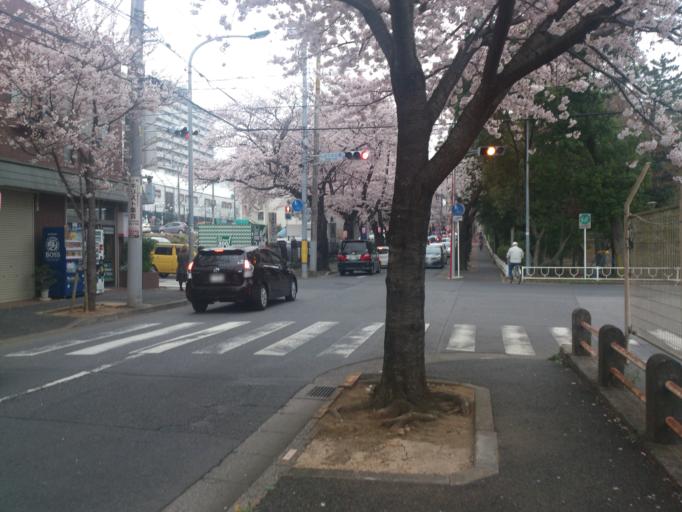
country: JP
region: Chiba
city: Matsudo
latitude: 35.8018
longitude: 139.9485
